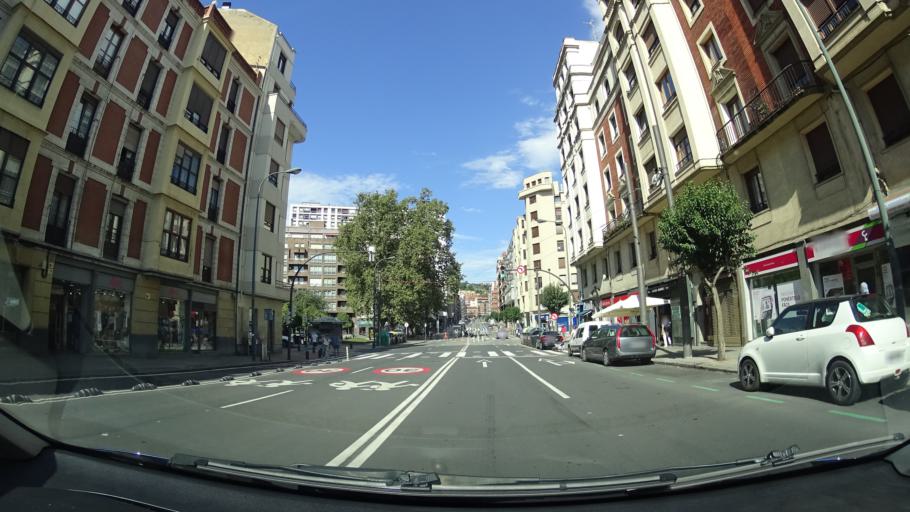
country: ES
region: Basque Country
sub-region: Bizkaia
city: Bilbao
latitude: 43.2577
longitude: -2.9431
